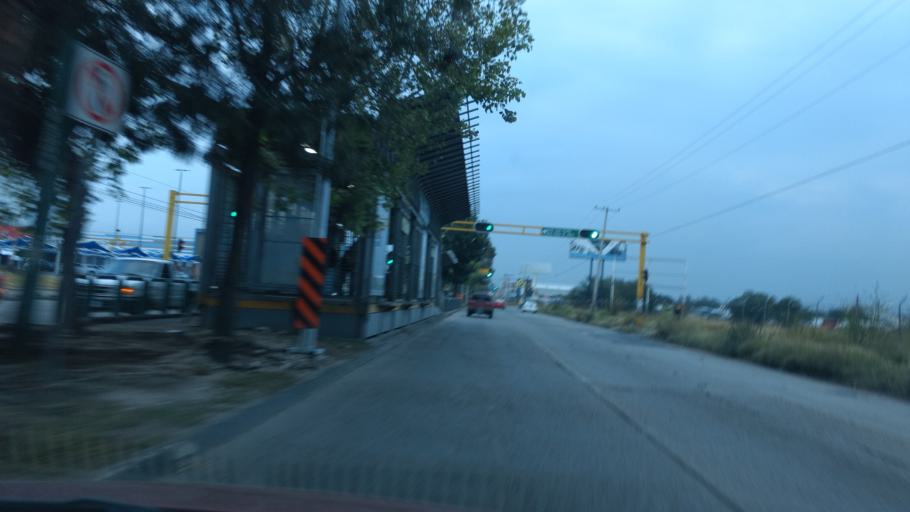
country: MX
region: Guanajuato
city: Leon
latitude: 21.0977
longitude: -101.6620
